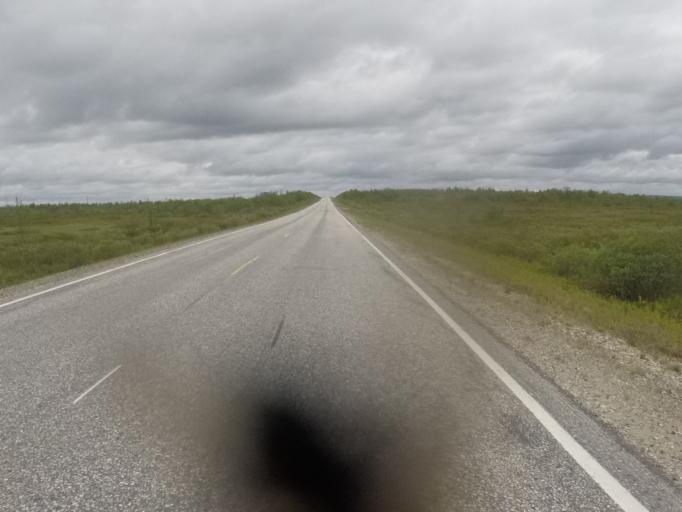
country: NO
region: Finnmark Fylke
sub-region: Kautokeino
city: Kautokeino
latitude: 68.7917
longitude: 23.2965
